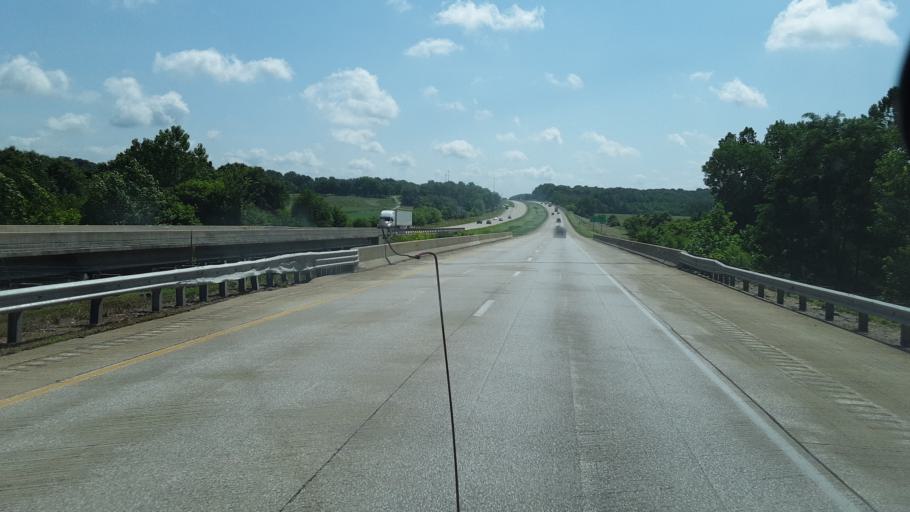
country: US
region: Illinois
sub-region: Clark County
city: Marshall
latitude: 39.4227
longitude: -87.6744
